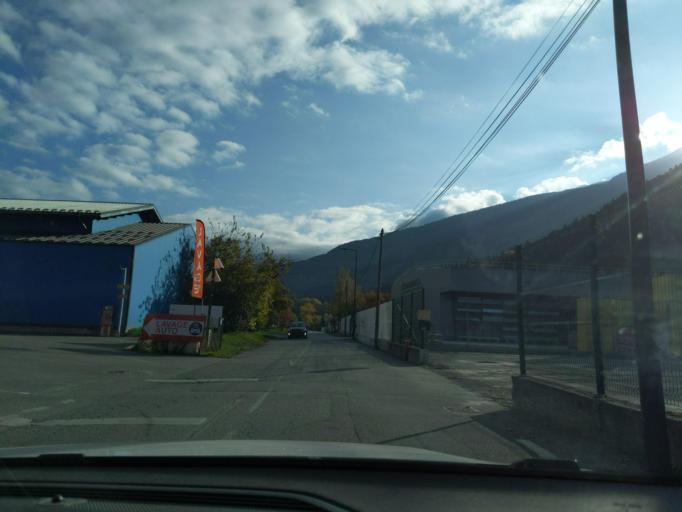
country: FR
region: Rhone-Alpes
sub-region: Departement de la Savoie
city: Aime
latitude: 45.5503
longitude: 6.6421
